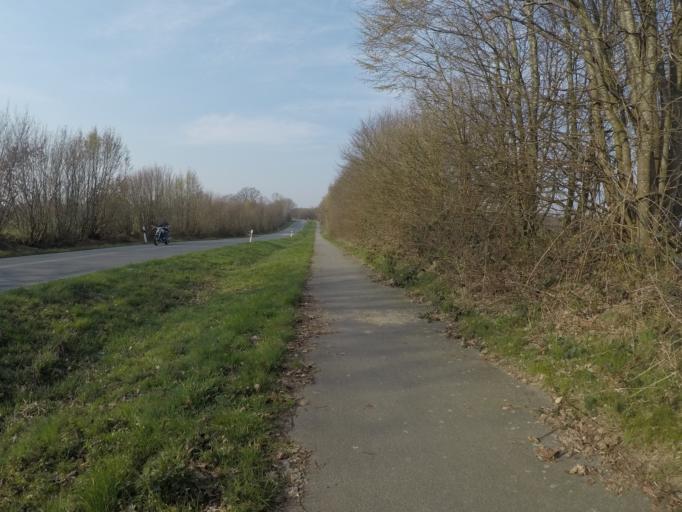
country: DE
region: Schleswig-Holstein
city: Kukels
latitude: 53.9084
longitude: 10.2303
